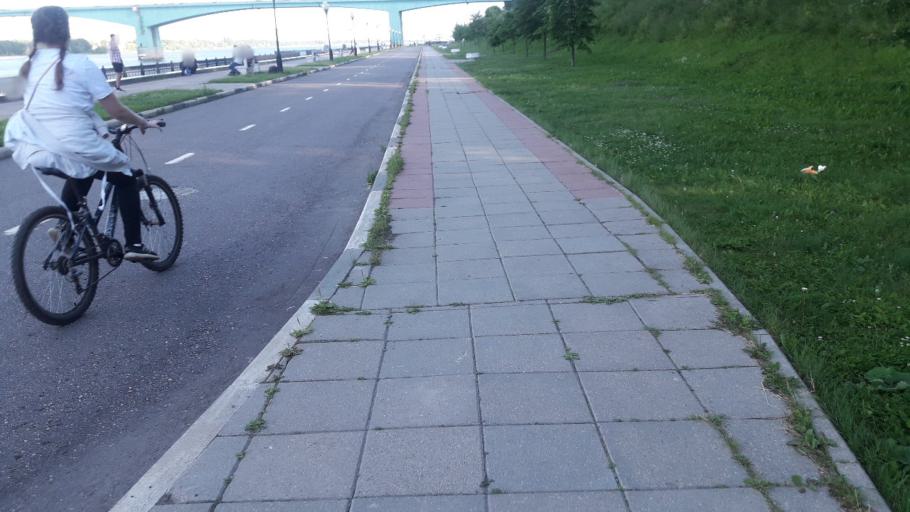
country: RU
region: Jaroslavl
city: Yaroslavl
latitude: 57.6427
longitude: 39.8857
